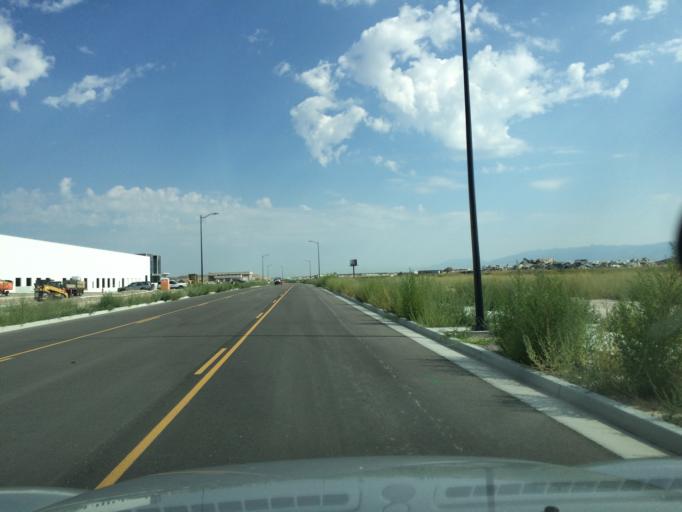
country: US
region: Utah
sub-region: Salt Lake County
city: Magna
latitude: 40.7158
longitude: -112.0525
